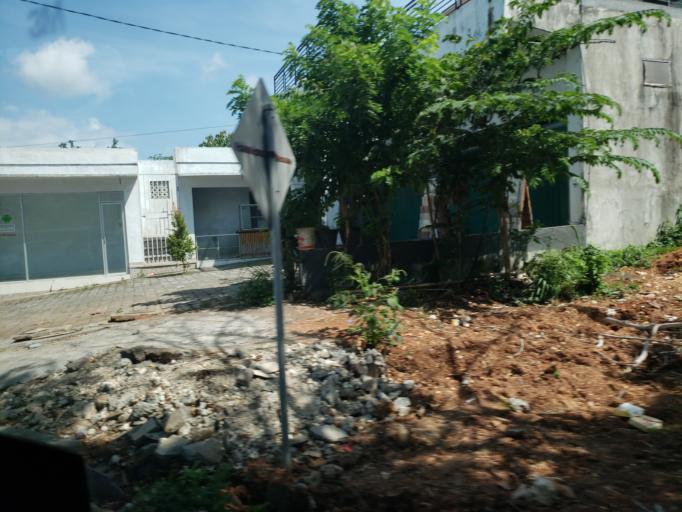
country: ID
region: Bali
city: Kangin
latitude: -8.8201
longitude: 115.1512
